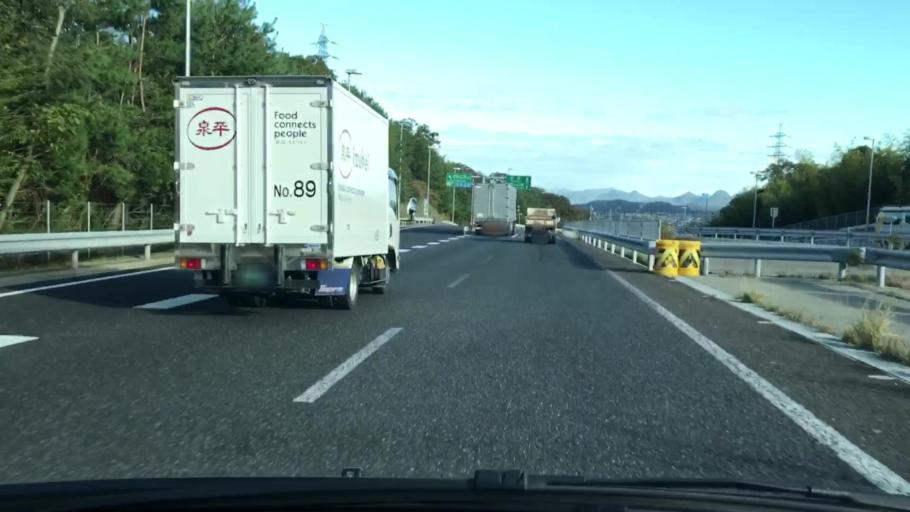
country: JP
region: Hyogo
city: Sandacho
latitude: 34.8130
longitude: 135.2471
